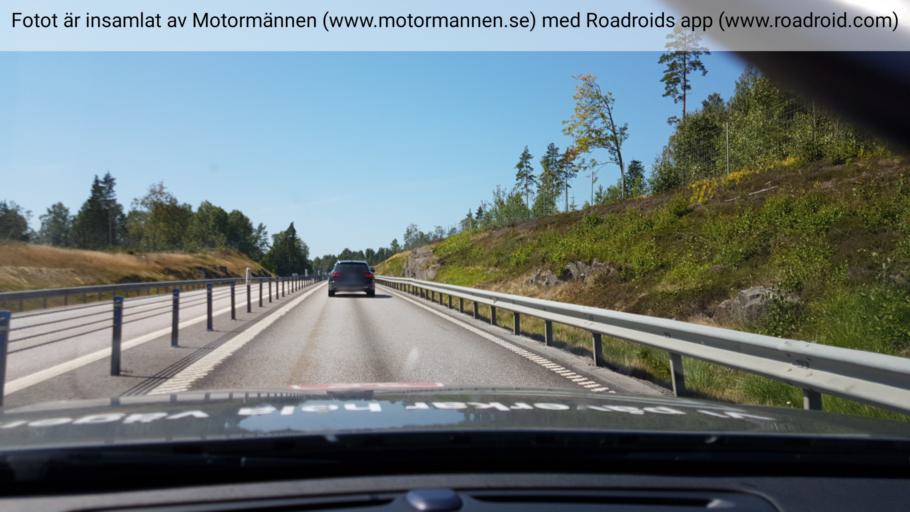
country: SE
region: OErebro
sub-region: Laxa Kommun
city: Laxa
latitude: 58.9756
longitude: 14.5582
